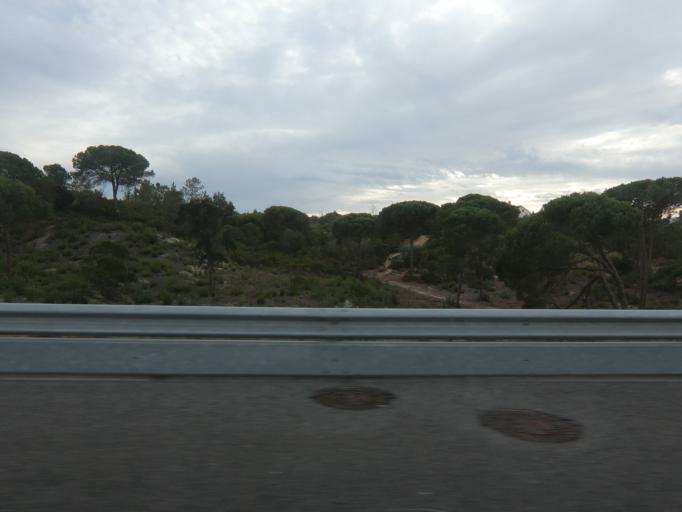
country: PT
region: Setubal
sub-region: Almada
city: Charneca
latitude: 38.6212
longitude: -9.1833
